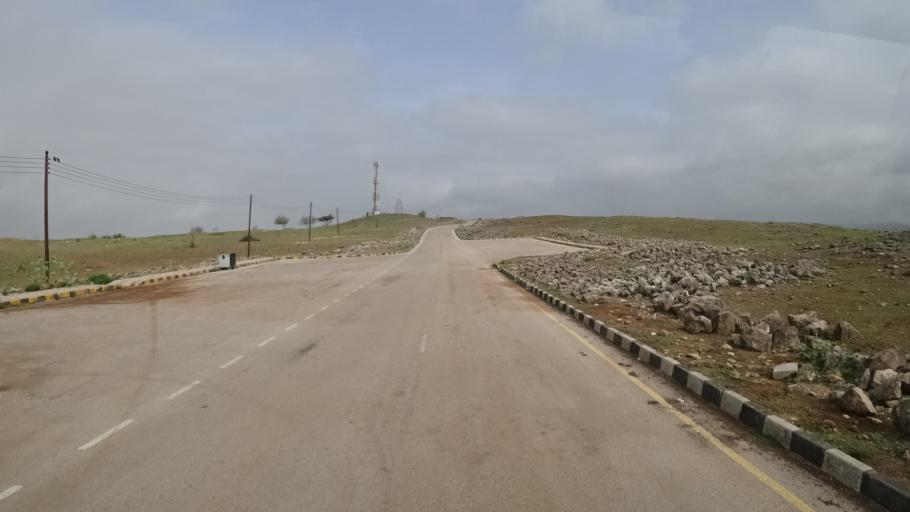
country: OM
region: Zufar
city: Salalah
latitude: 17.0779
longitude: 54.4479
